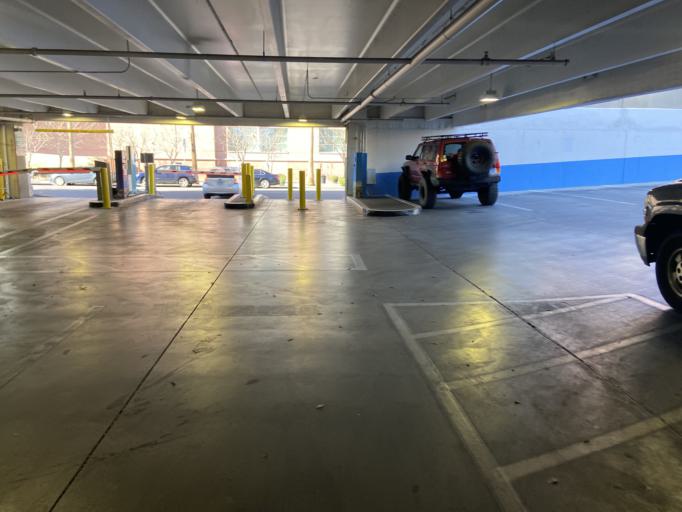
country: US
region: Nevada
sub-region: Clark County
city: Las Vegas
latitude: 36.1659
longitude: -115.1454
